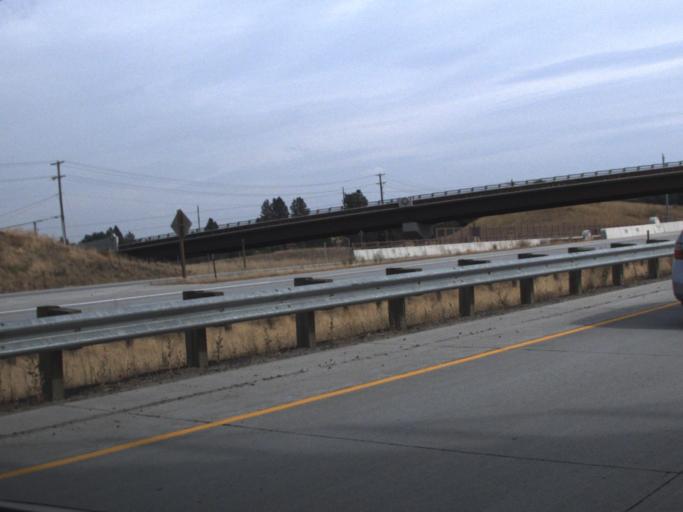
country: US
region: Washington
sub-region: Spokane County
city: Mead
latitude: 47.7763
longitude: -117.3742
